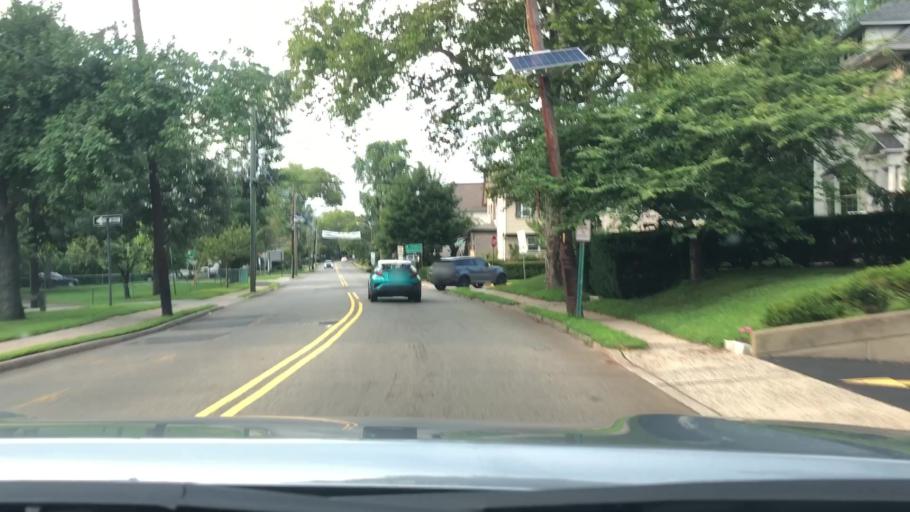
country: US
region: New Jersey
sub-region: Bergen County
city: Ridgefield Park
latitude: 40.8513
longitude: -74.0260
